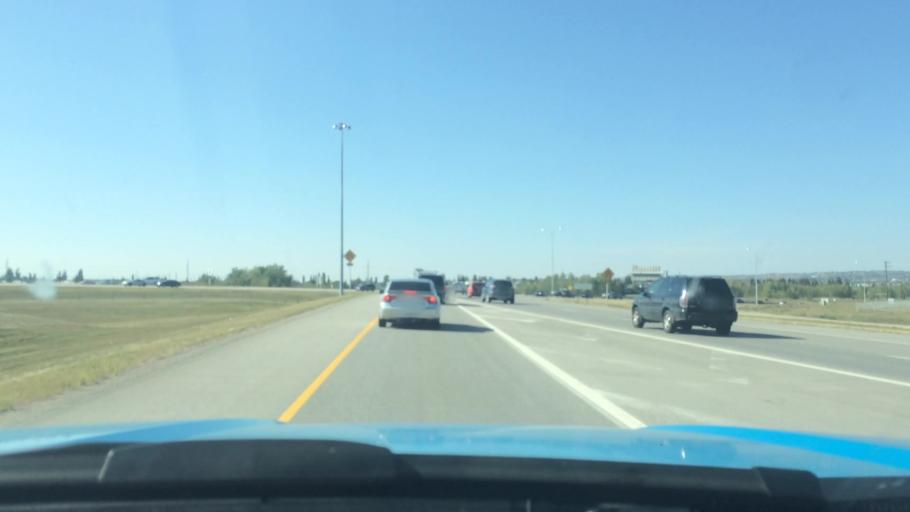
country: CA
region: Alberta
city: Calgary
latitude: 51.0903
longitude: -114.2307
